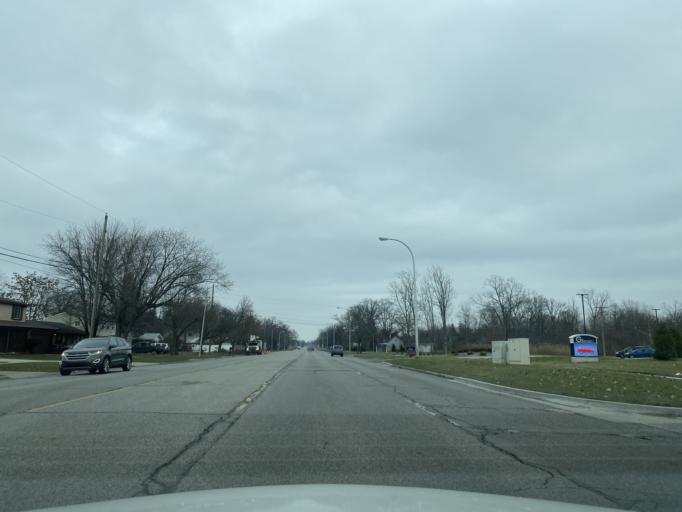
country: US
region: Michigan
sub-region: Wayne County
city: Taylor
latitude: 42.2261
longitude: -83.2814
